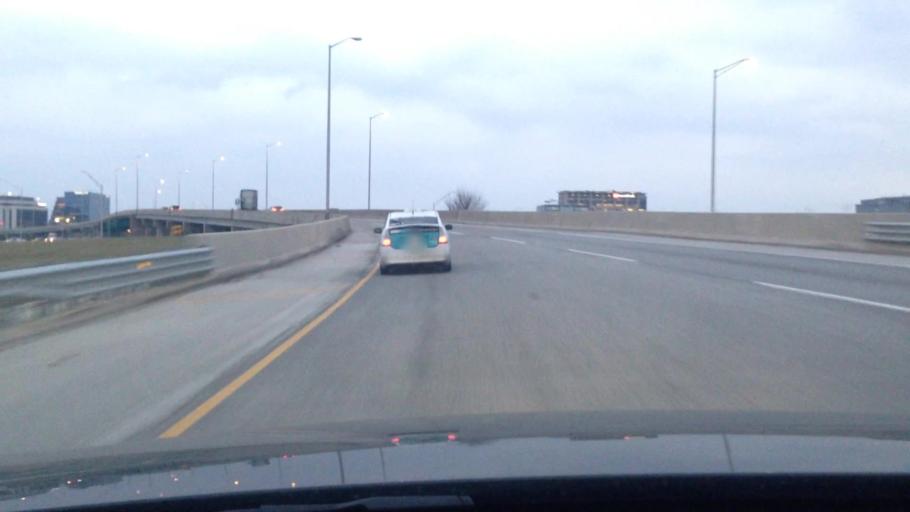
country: US
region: Illinois
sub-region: Cook County
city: Rosemont
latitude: 41.9872
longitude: -87.8667
